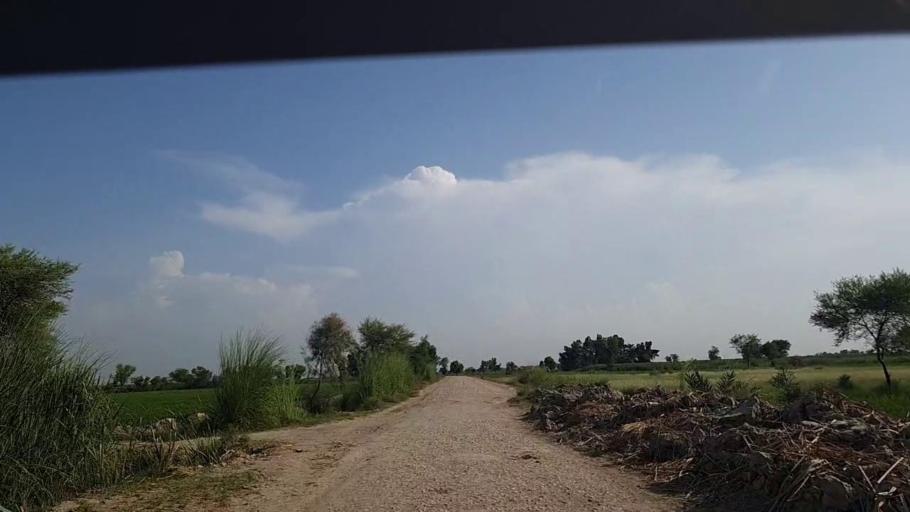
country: PK
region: Sindh
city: Khanpur
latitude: 27.8665
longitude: 69.3750
